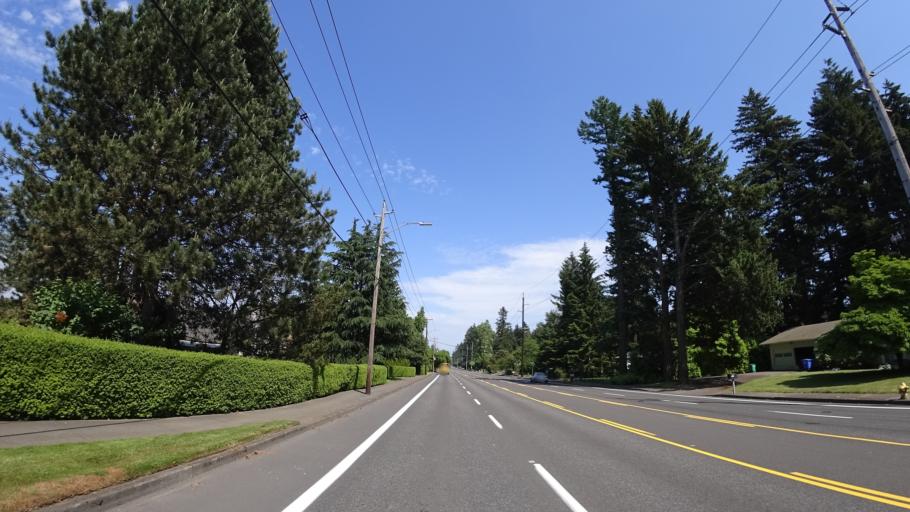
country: US
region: Oregon
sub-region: Multnomah County
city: Fairview
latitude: 45.5337
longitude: -122.5075
